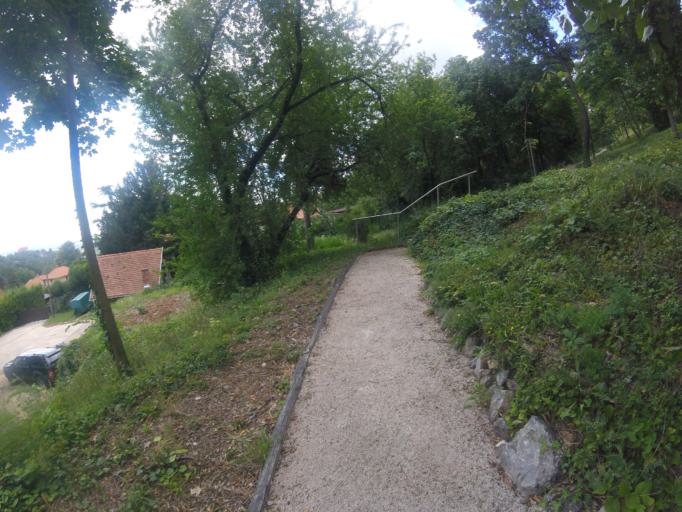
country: HU
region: Baranya
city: Pecs
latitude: 46.0881
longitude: 18.2330
